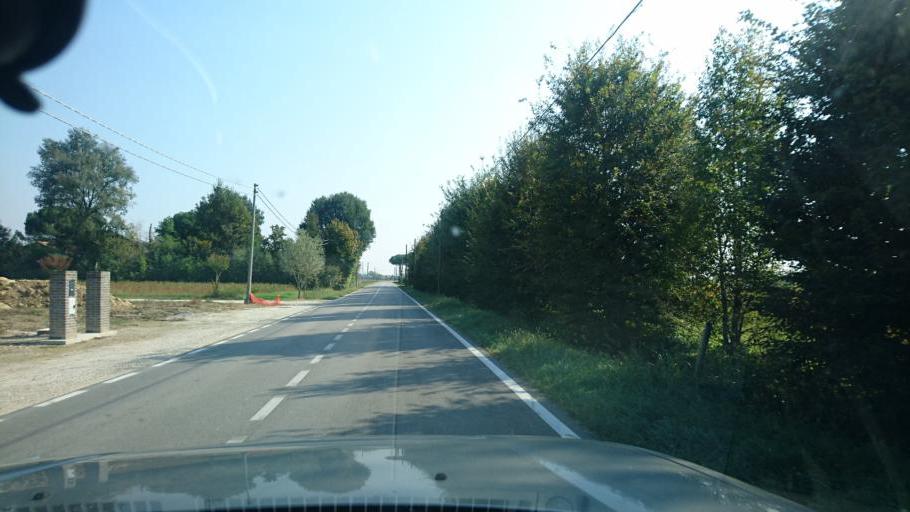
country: IT
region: Veneto
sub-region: Provincia di Padova
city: Ronchi di Campanile
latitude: 45.4781
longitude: 11.7780
